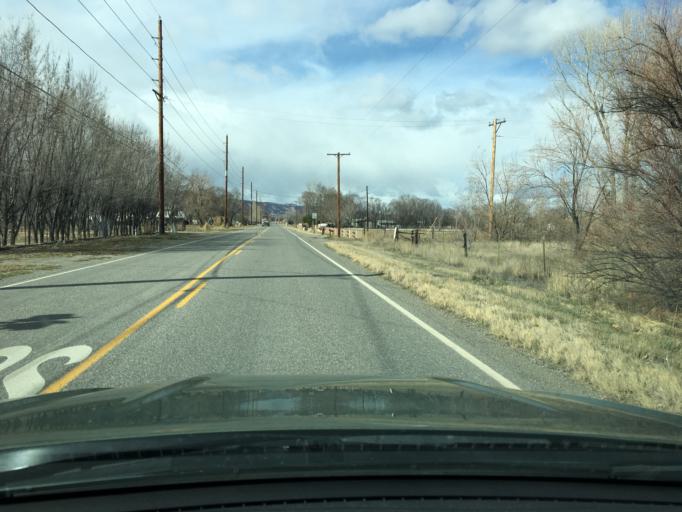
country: US
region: Colorado
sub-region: Mesa County
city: Redlands
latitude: 39.1209
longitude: -108.6184
